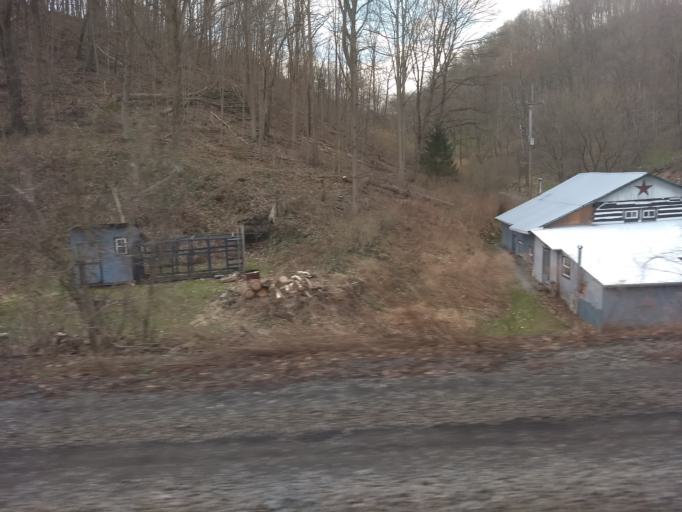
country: US
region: Pennsylvania
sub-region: Blair County
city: Tyrone
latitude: 40.6545
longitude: -78.2068
